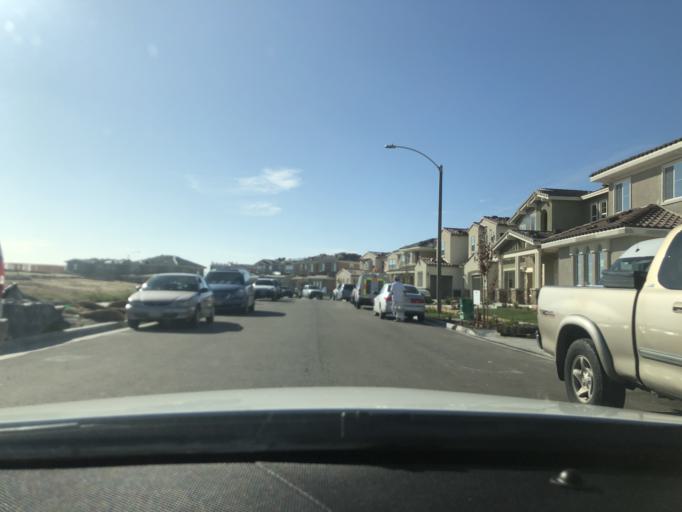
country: US
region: California
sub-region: San Diego County
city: Bonita
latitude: 32.6104
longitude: -116.9908
